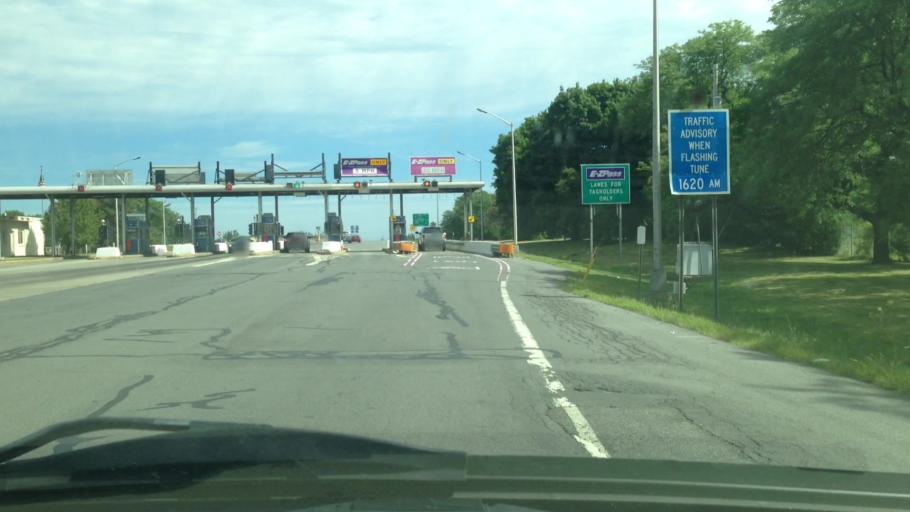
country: US
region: New York
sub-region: Onondaga County
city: East Syracuse
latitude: 43.0895
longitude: -76.0896
